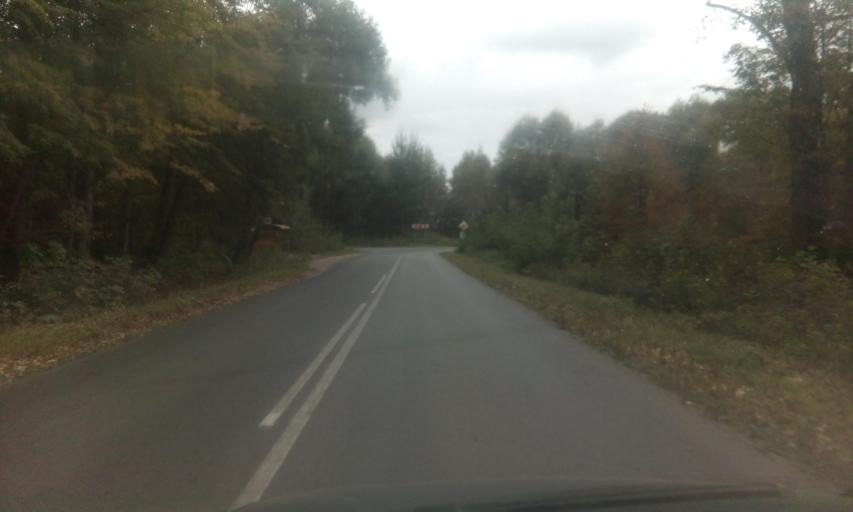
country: RU
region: Tula
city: Partizan
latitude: 53.9614
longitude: 38.0869
